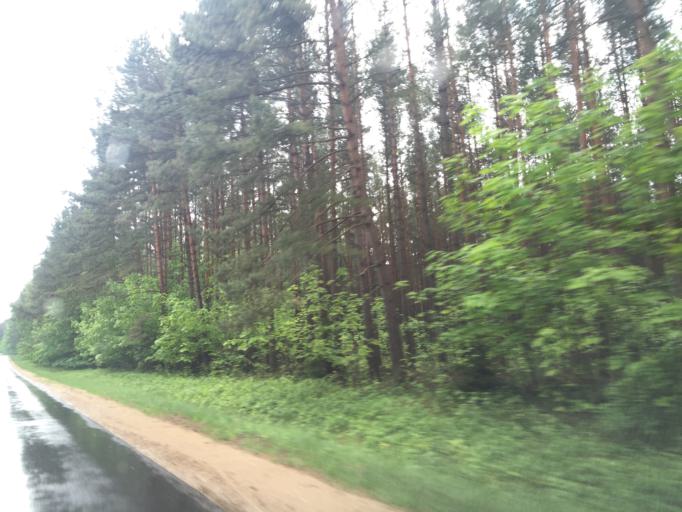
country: LT
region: Klaipedos apskritis
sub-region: Klaipeda
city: Klaipeda
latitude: 55.7893
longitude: 21.0733
